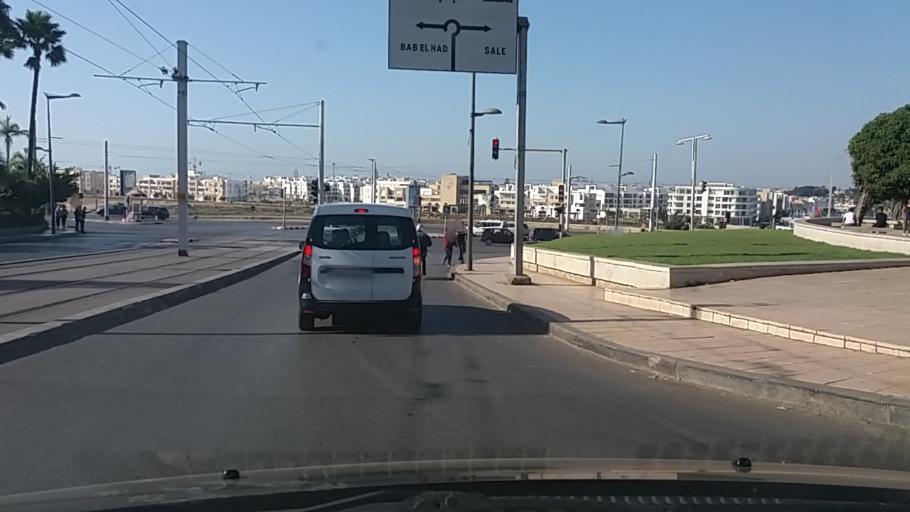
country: MA
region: Rabat-Sale-Zemmour-Zaer
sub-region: Rabat
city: Rabat
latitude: 34.0255
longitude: -6.8253
